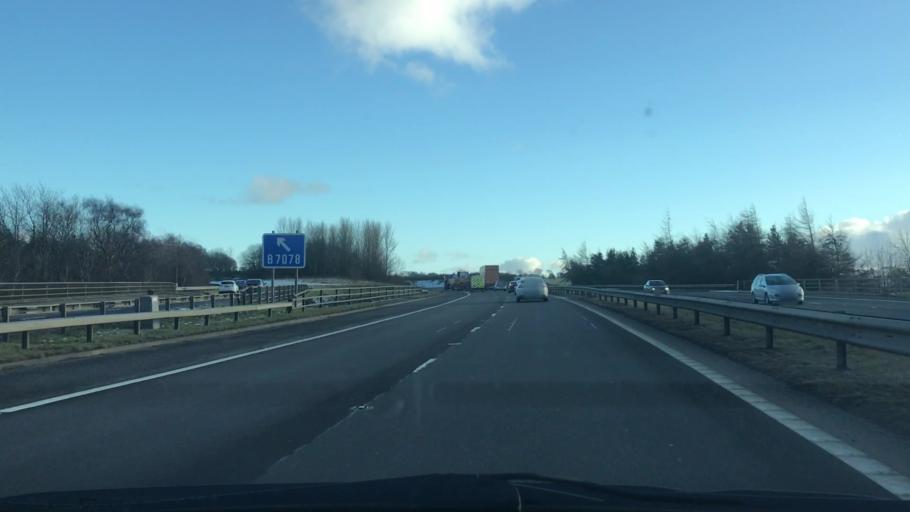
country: GB
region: Scotland
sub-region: South Lanarkshire
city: Blackwood
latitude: 55.6651
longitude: -3.9249
